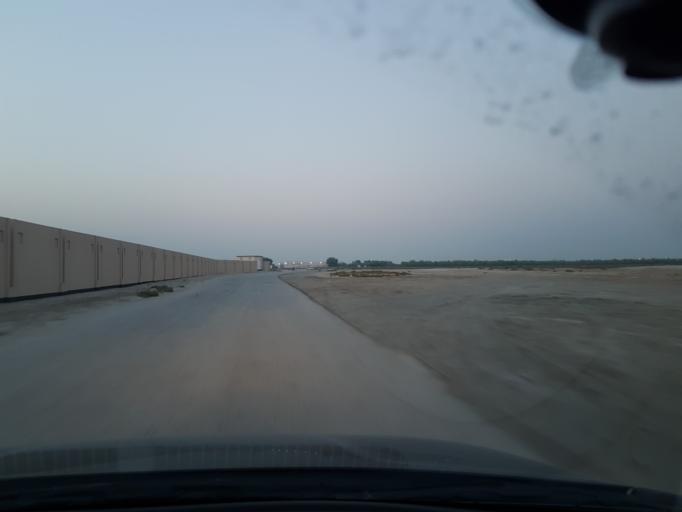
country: BH
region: Central Governorate
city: Dar Kulayb
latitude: 26.0079
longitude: 50.4752
